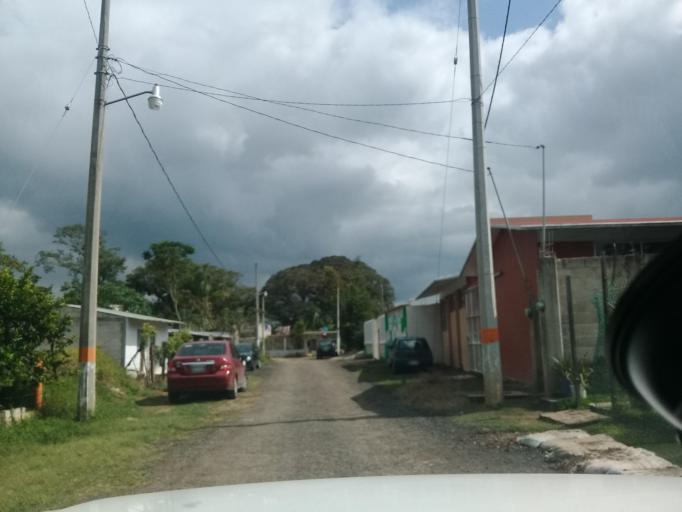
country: MX
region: Veracruz
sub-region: Xalapa
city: Fraccionamiento las Fuentes
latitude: 19.4737
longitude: -96.8773
